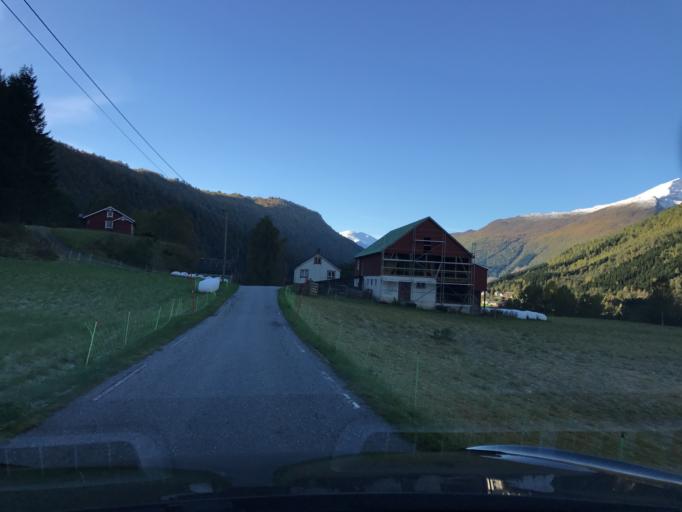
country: NO
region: More og Romsdal
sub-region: Norddal
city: Valldal
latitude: 62.3262
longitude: 7.3340
